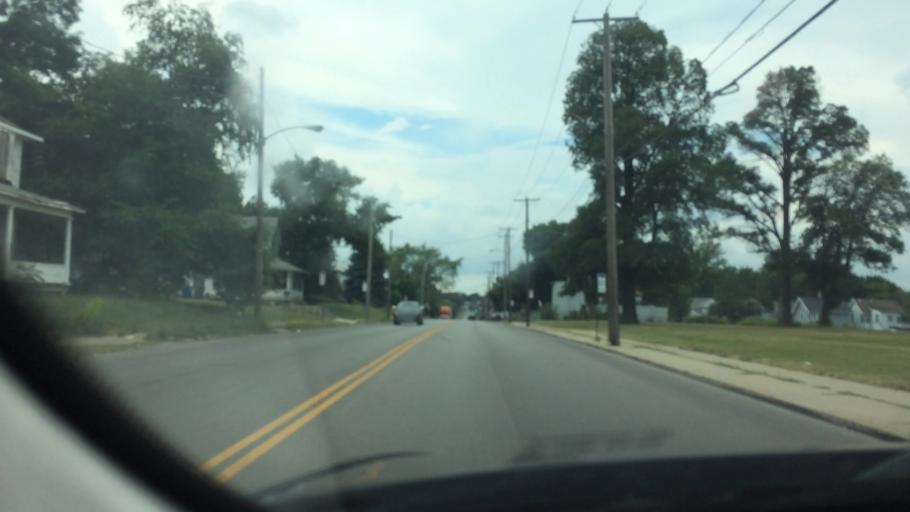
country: US
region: Ohio
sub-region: Wood County
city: Rossford
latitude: 41.6347
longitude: -83.5707
